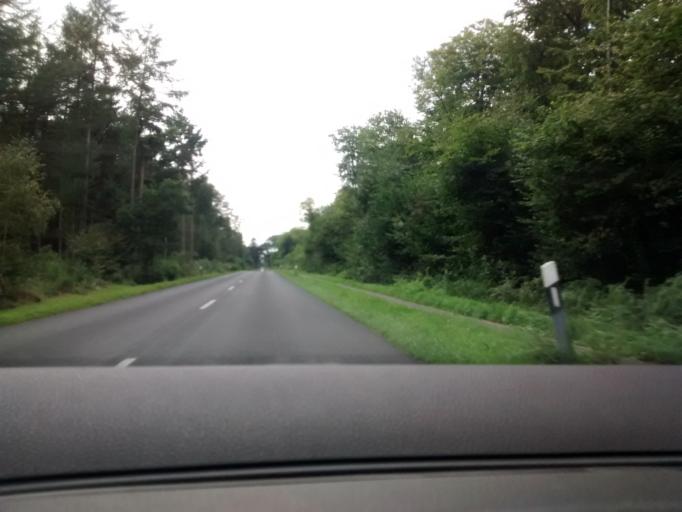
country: DE
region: Lower Saxony
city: Brietlingen
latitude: 53.3163
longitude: 10.4830
